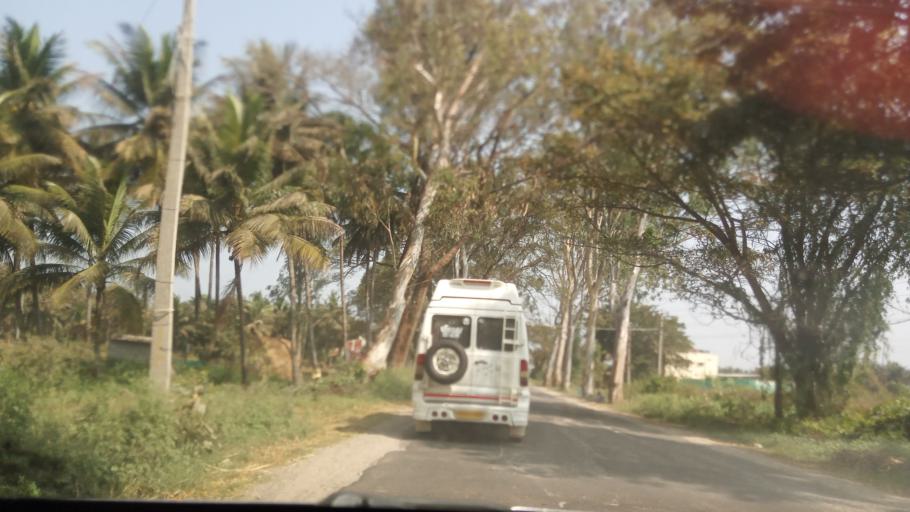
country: IN
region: Karnataka
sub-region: Mandya
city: Shrirangapattana
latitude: 12.4030
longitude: 76.6444
